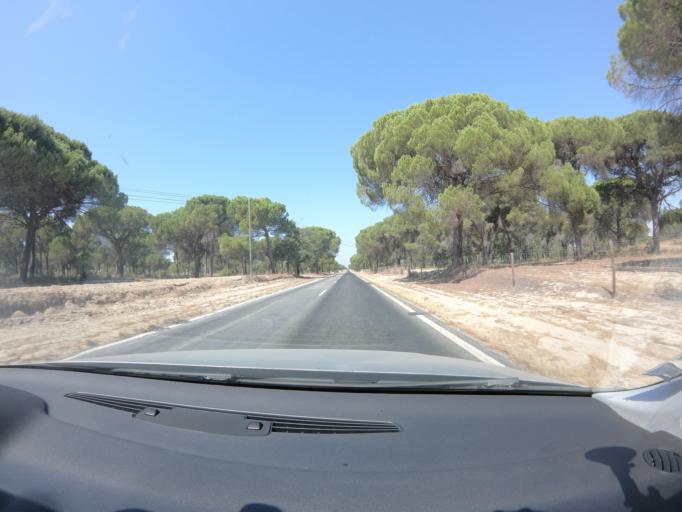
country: PT
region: Setubal
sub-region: Alcacer do Sal
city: Alcacer do Sal
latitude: 38.3788
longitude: -8.5573
